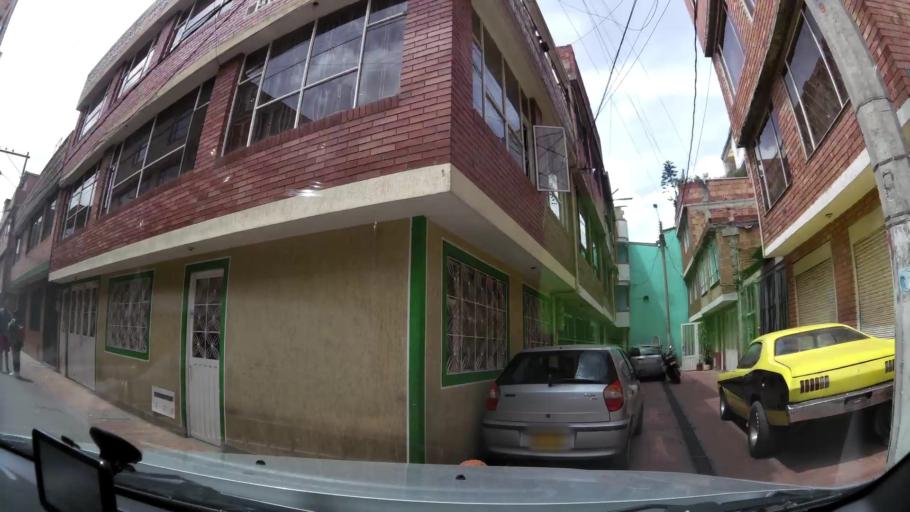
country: CO
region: Bogota D.C.
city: Bogota
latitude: 4.6534
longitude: -74.1321
